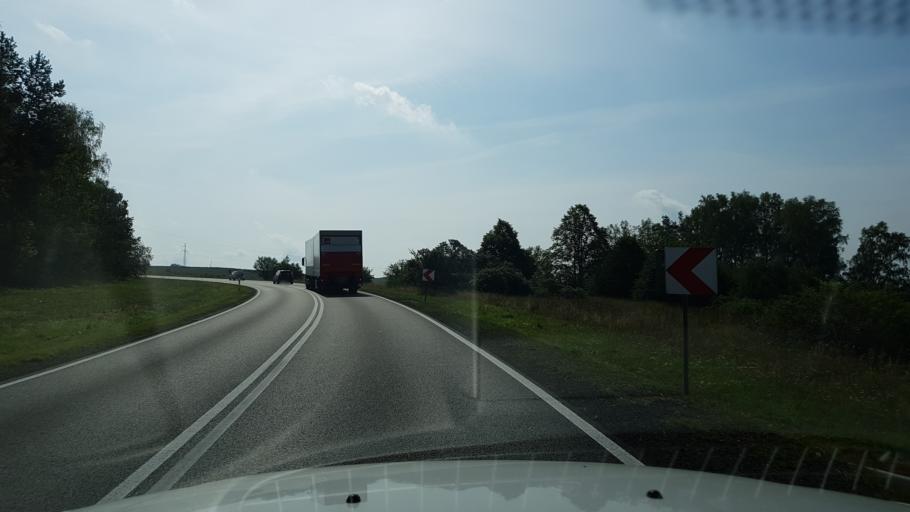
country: PL
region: West Pomeranian Voivodeship
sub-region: Powiat walecki
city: Miroslawiec
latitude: 53.3412
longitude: 16.2423
